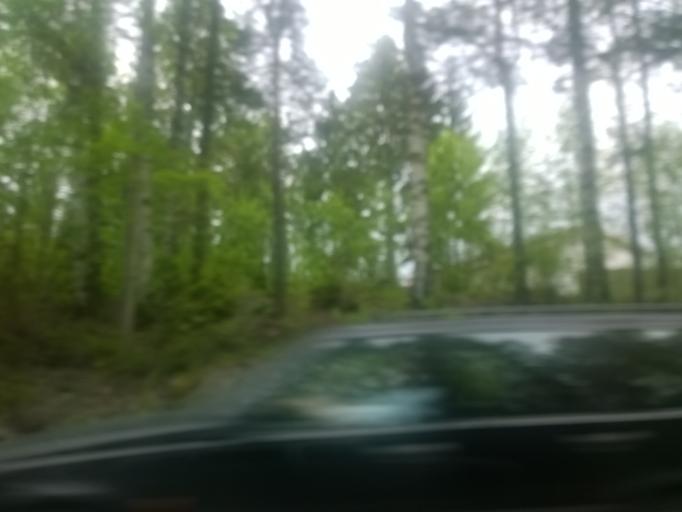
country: FI
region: Pirkanmaa
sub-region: Tampere
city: Lempaeaelae
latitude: 61.3371
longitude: 23.7525
